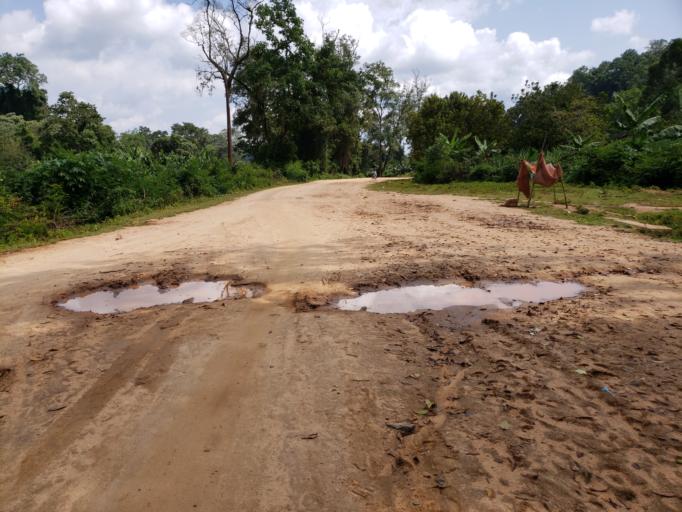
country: ET
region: Oromiya
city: Dodola
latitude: 6.4530
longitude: 39.5695
